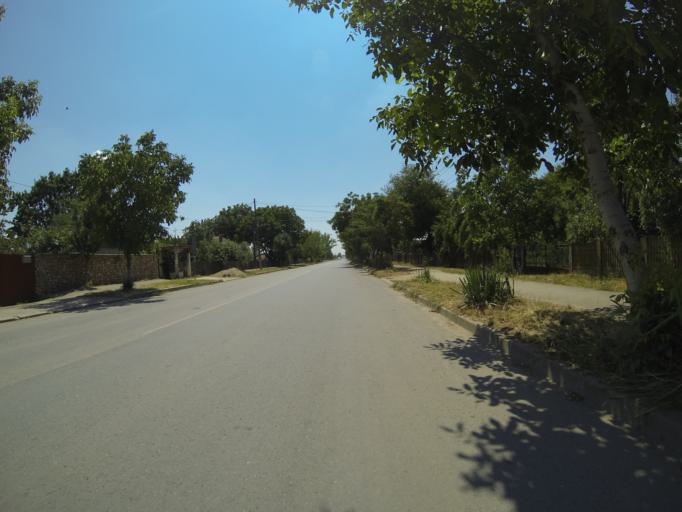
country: RO
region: Dolj
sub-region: Comuna Segarcea
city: Segarcea
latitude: 44.0886
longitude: 23.7288
